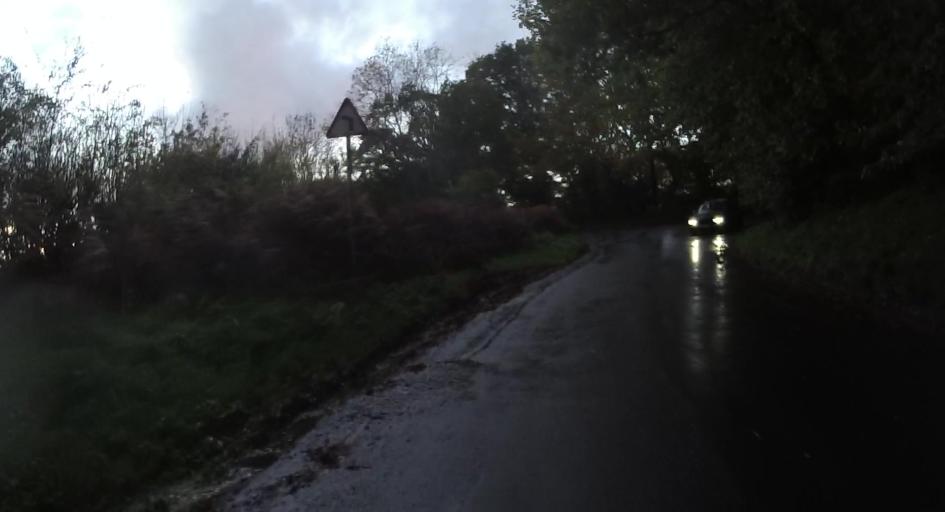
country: GB
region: England
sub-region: Hampshire
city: Long Sutton
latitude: 51.2002
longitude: -0.9396
